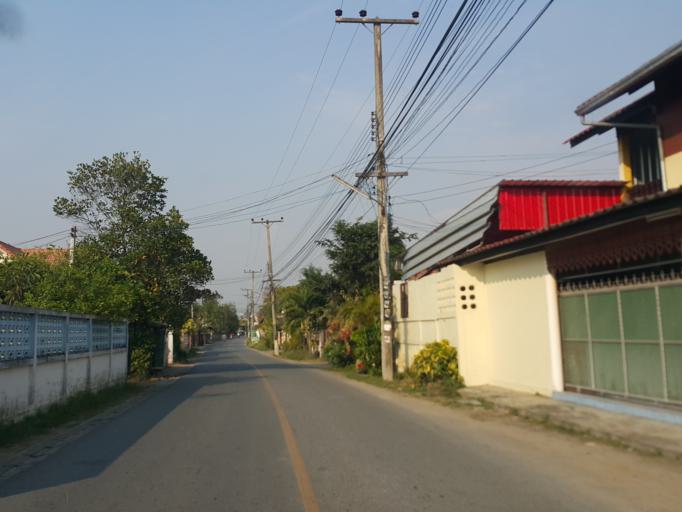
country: TH
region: Chiang Mai
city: San Kamphaeng
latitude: 18.7523
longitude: 99.1261
